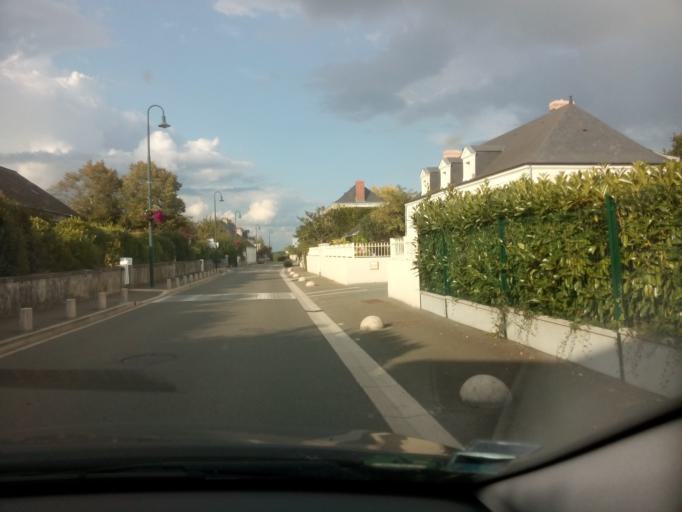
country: FR
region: Pays de la Loire
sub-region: Departement de Maine-et-Loire
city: Soulaire-et-Bourg
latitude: 47.5780
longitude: -0.5541
